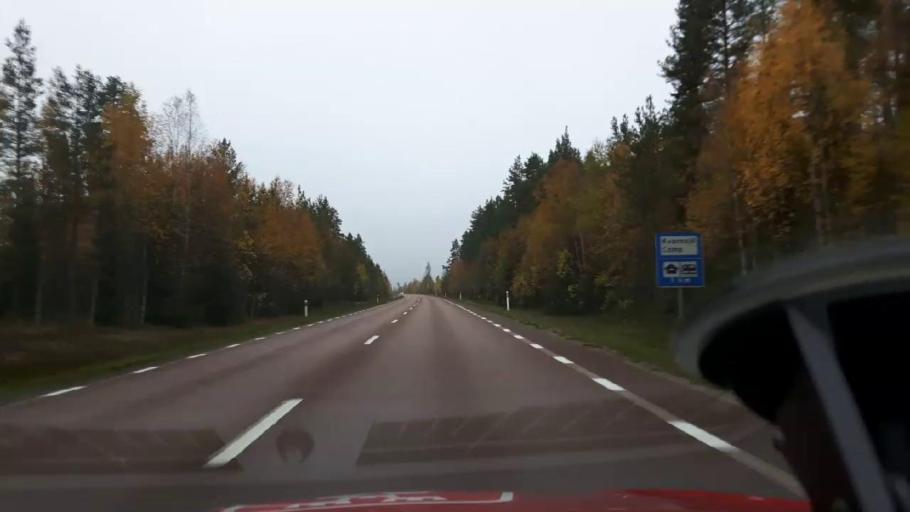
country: SE
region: Jaemtland
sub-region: Bergs Kommun
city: Hoverberg
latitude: 62.5373
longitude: 14.4485
